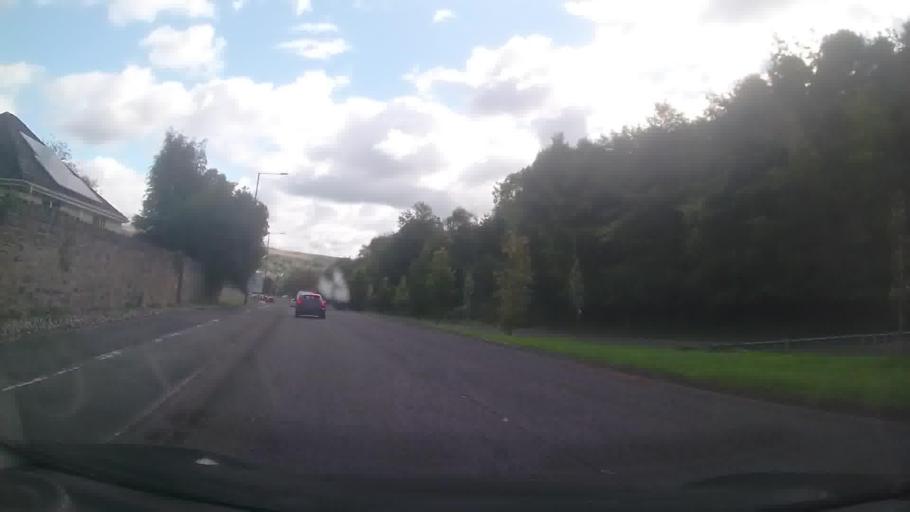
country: GB
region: Wales
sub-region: Merthyr Tydfil County Borough
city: Merthyr Tydfil
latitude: 51.7509
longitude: -3.3902
